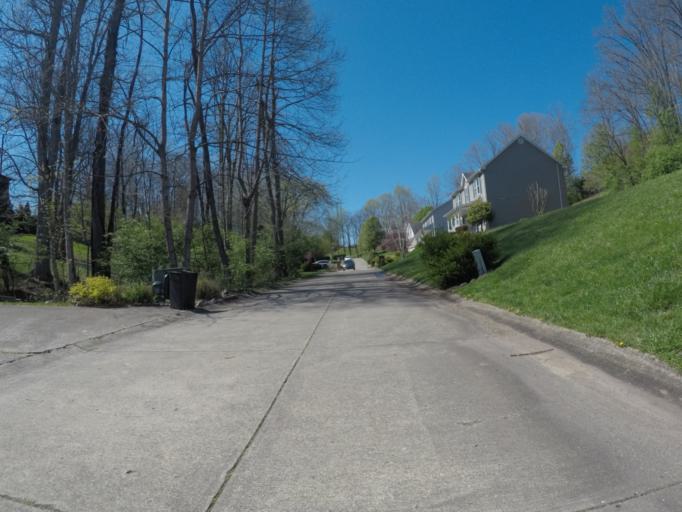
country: US
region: West Virginia
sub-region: Cabell County
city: Pea Ridge
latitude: 38.4150
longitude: -82.3129
